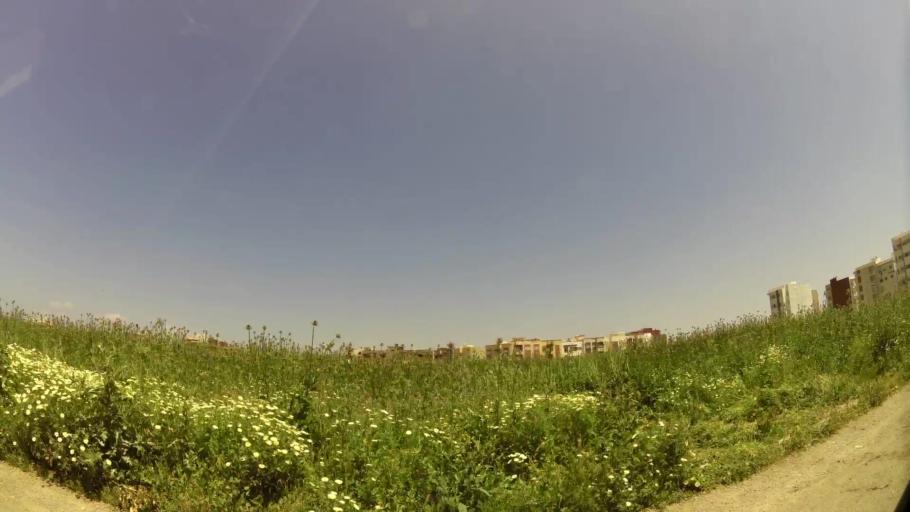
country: MA
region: Fes-Boulemane
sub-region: Fes
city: Fes
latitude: 34.0313
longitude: -5.0419
